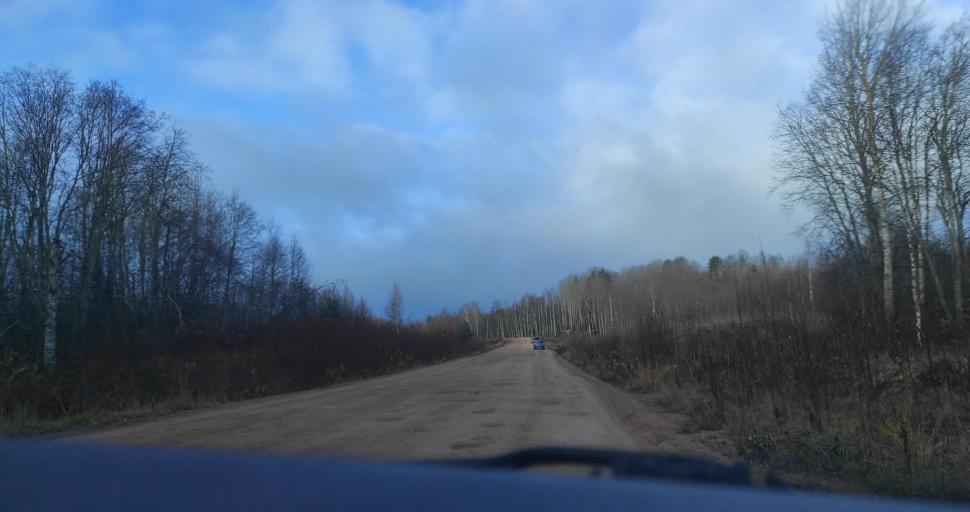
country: RU
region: Republic of Karelia
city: Pitkyaranta
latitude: 61.7123
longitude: 31.3569
